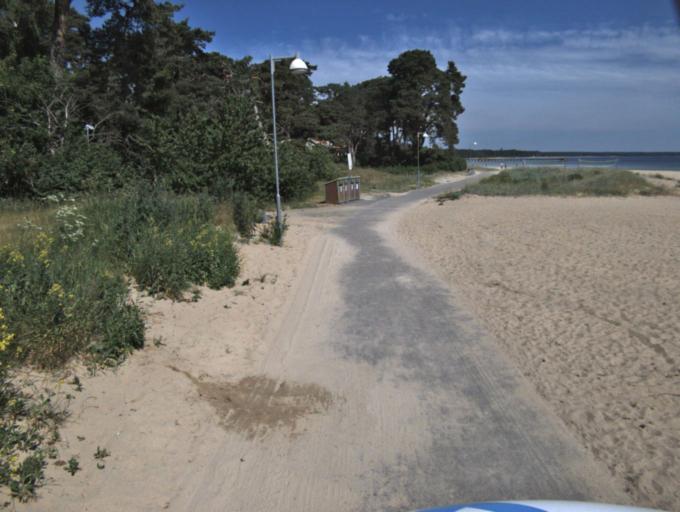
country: SE
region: Skane
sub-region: Kristianstads Kommun
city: Ahus
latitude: 55.9326
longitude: 14.3201
